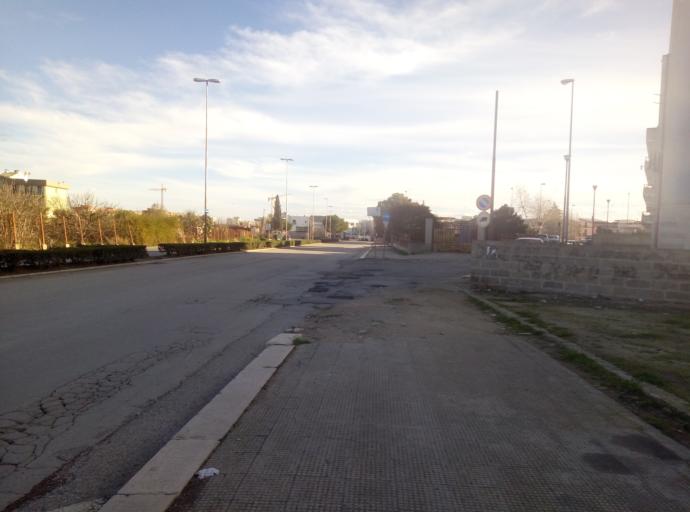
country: IT
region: Apulia
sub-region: Provincia di Bari
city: Ruvo di Puglia
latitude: 41.1186
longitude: 16.4918
